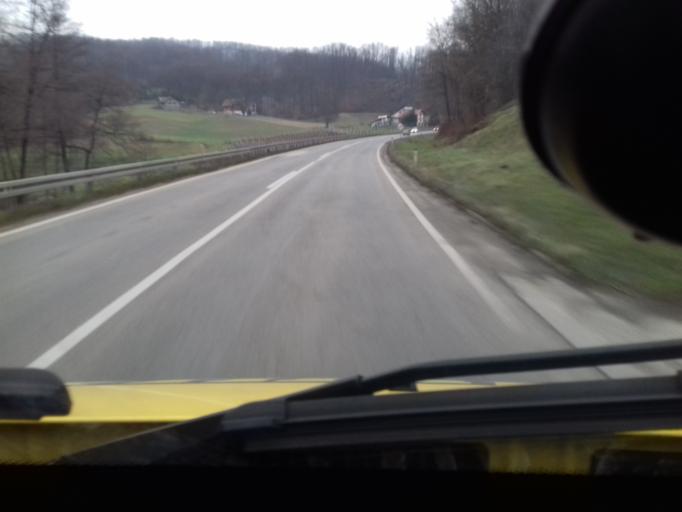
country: BA
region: Federation of Bosnia and Herzegovina
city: Lijesnica
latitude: 44.4744
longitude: 18.0690
